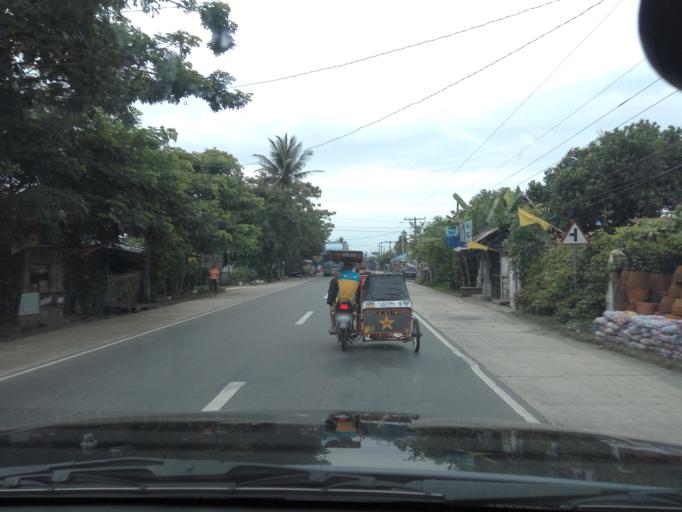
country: PH
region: Central Luzon
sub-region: Province of Nueva Ecija
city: Carmen
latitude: 15.4470
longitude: 120.8189
